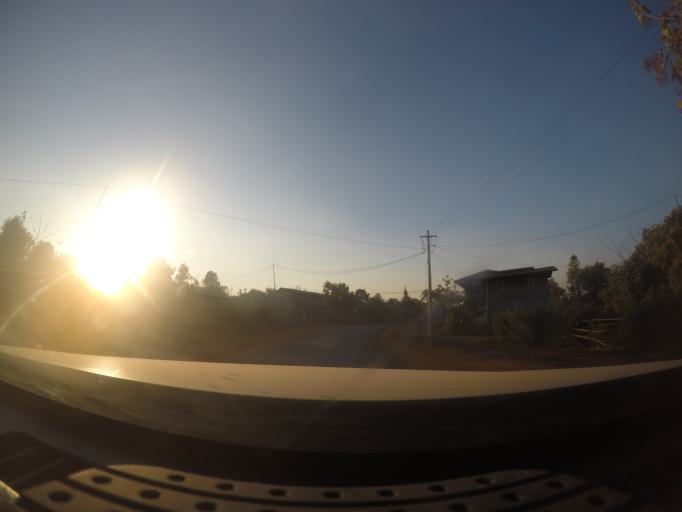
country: MM
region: Shan
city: Taunggyi
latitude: 20.5037
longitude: 97.0866
